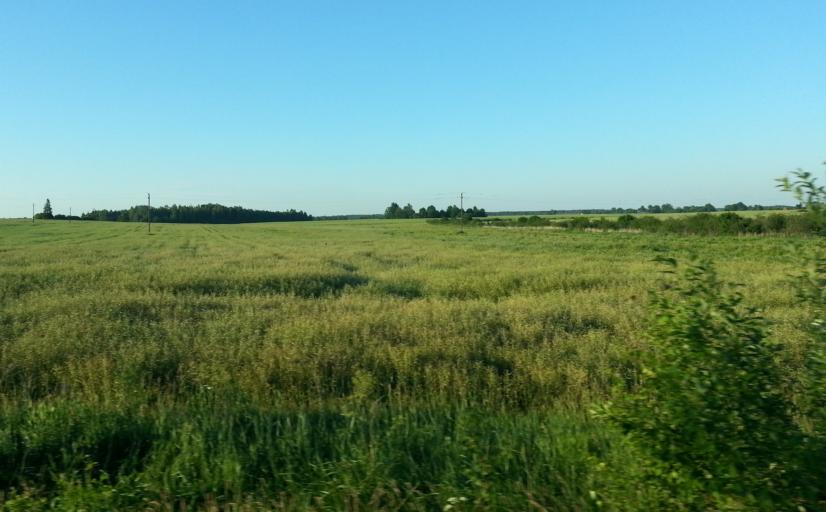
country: LT
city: Ramygala
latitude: 55.5993
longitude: 24.3517
